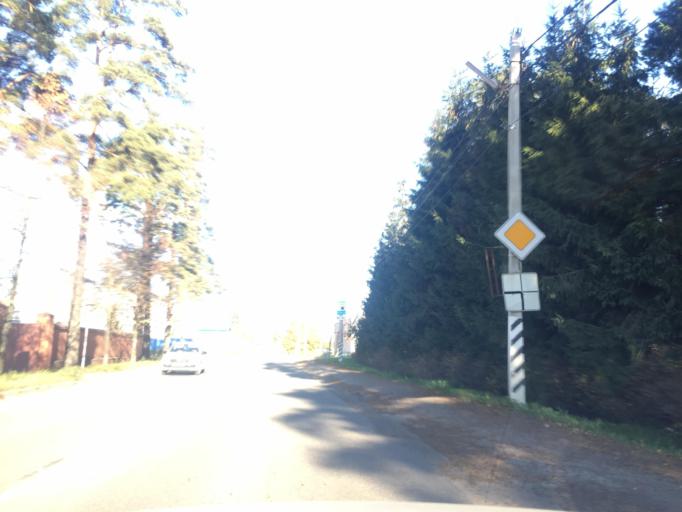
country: RU
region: Leningrad
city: Priozersk
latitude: 61.0430
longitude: 30.1205
